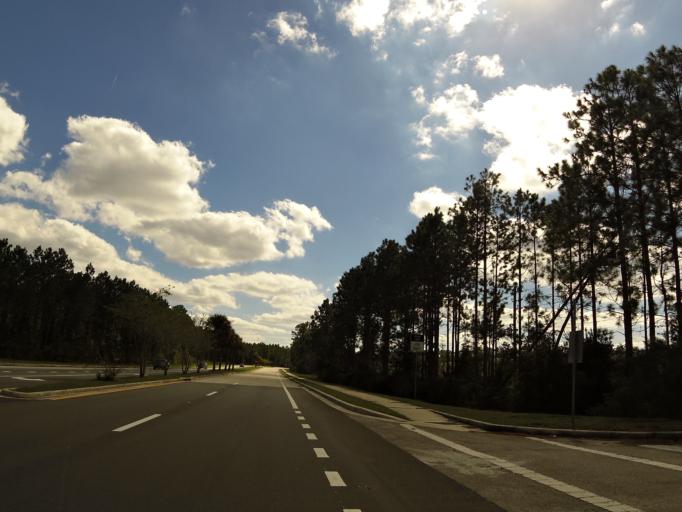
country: US
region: Florida
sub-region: Saint Johns County
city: Fruit Cove
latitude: 30.0735
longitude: -81.5323
